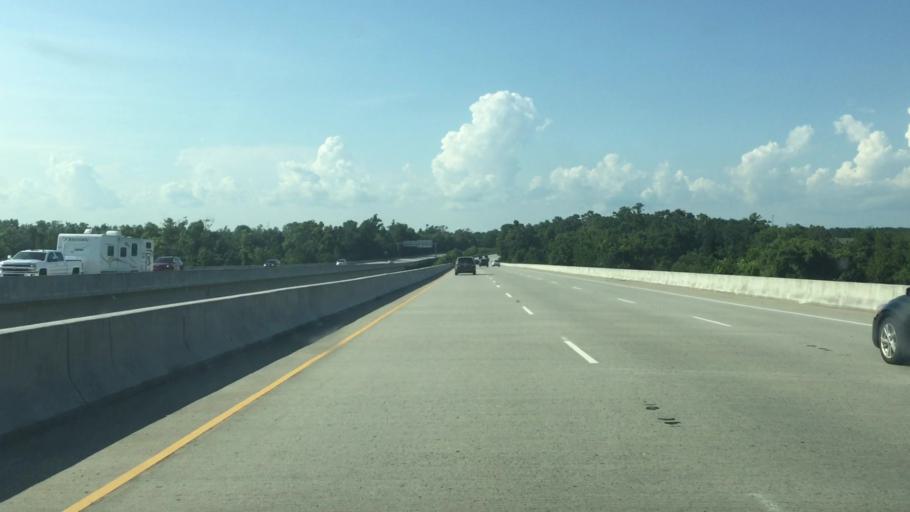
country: US
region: South Carolina
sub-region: Horry County
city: North Myrtle Beach
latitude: 33.7915
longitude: -78.7775
